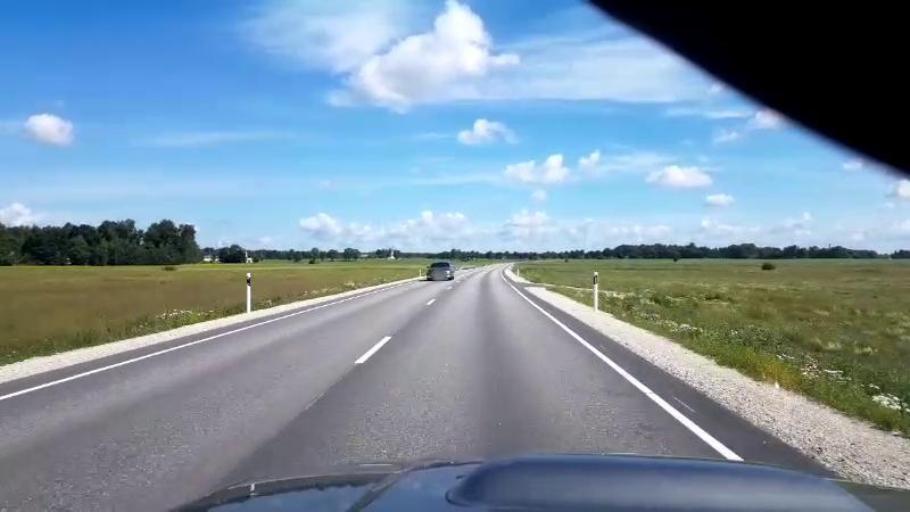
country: EE
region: Jaervamaa
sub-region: Jaerva-Jaani vald
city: Jarva-Jaani
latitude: 59.0868
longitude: 25.6866
